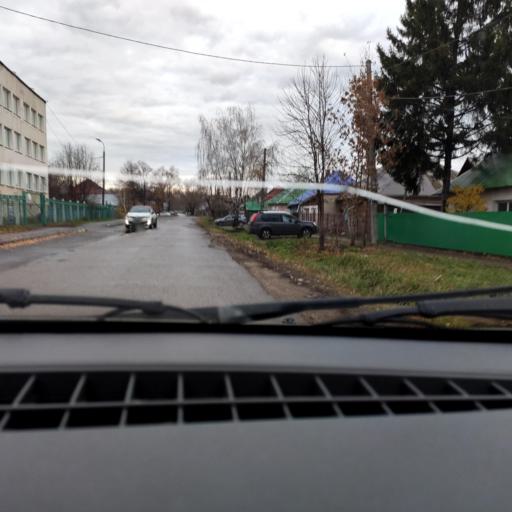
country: RU
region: Bashkortostan
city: Avdon
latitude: 54.6974
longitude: 55.8242
